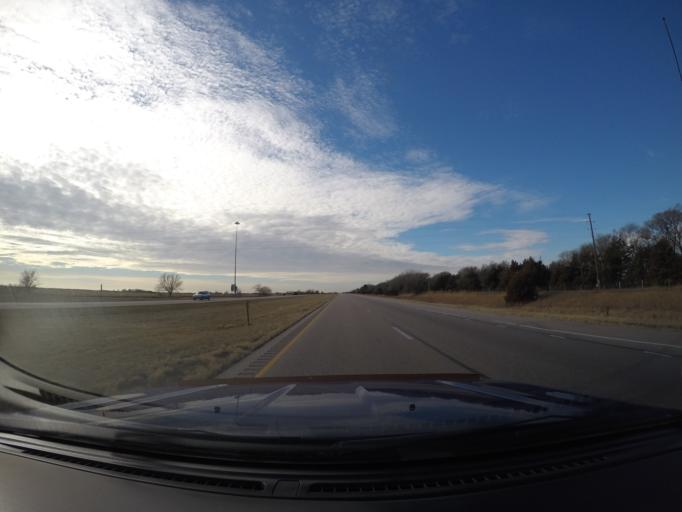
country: US
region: Nebraska
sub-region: Hall County
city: Grand Island
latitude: 40.8212
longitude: -98.2672
